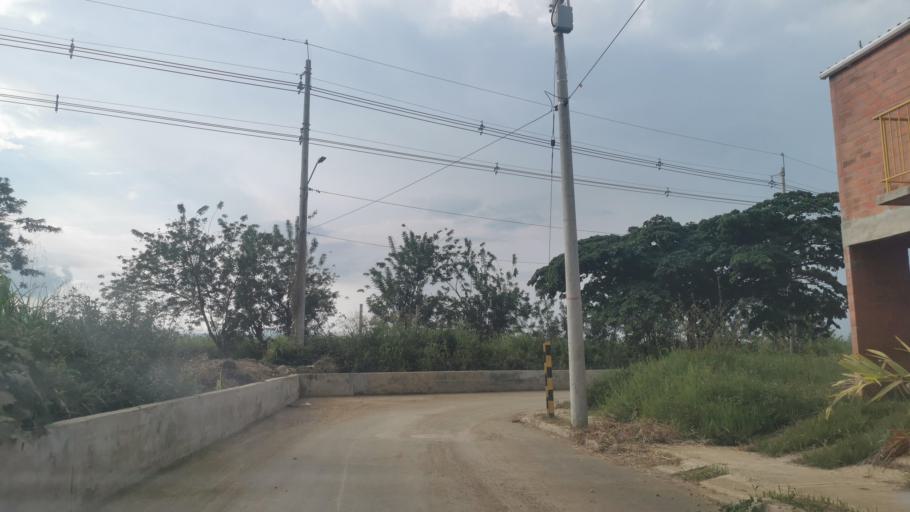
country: CO
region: Valle del Cauca
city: Jamundi
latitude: 3.2358
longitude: -76.5280
